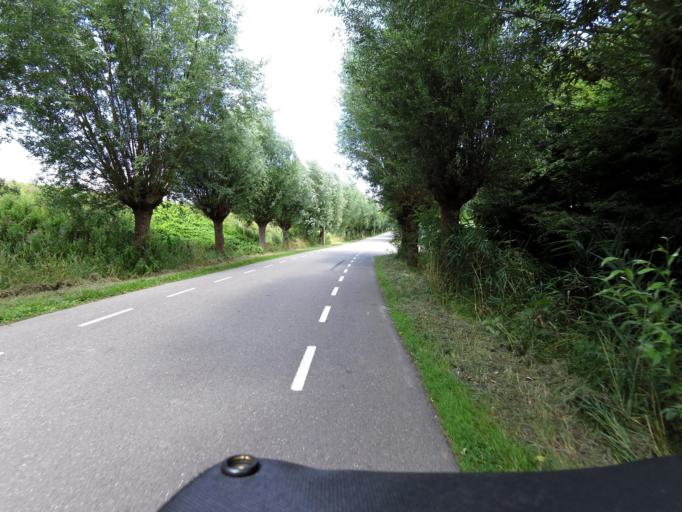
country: NL
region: North Brabant
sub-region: Gemeente Moerdijk
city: Willemstad
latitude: 51.7247
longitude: 4.4217
